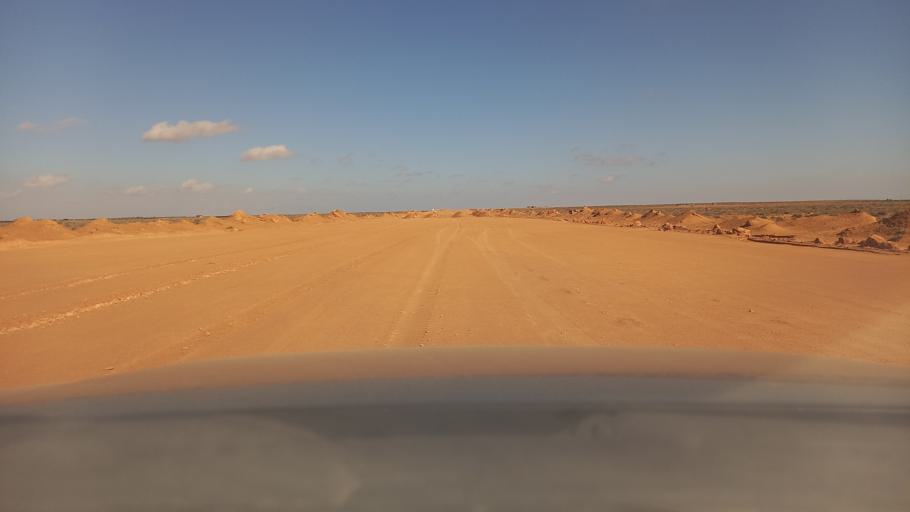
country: TN
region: Madanin
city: Medenine
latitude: 33.2381
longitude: 10.5533
